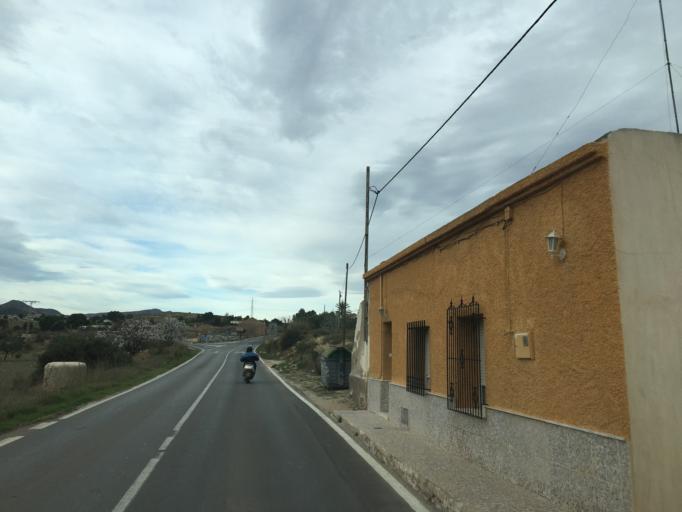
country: ES
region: Murcia
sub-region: Murcia
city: Cartagena
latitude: 37.6120
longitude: -1.0538
